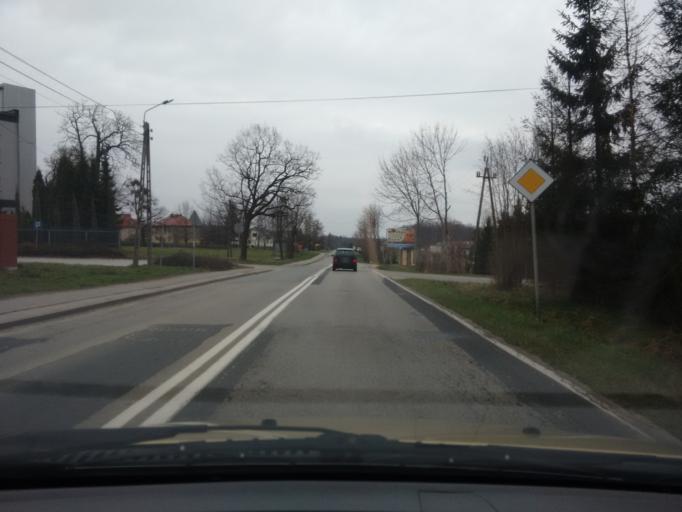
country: PL
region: Silesian Voivodeship
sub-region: Powiat pszczynski
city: Radostowice
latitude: 49.9802
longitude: 18.8902
